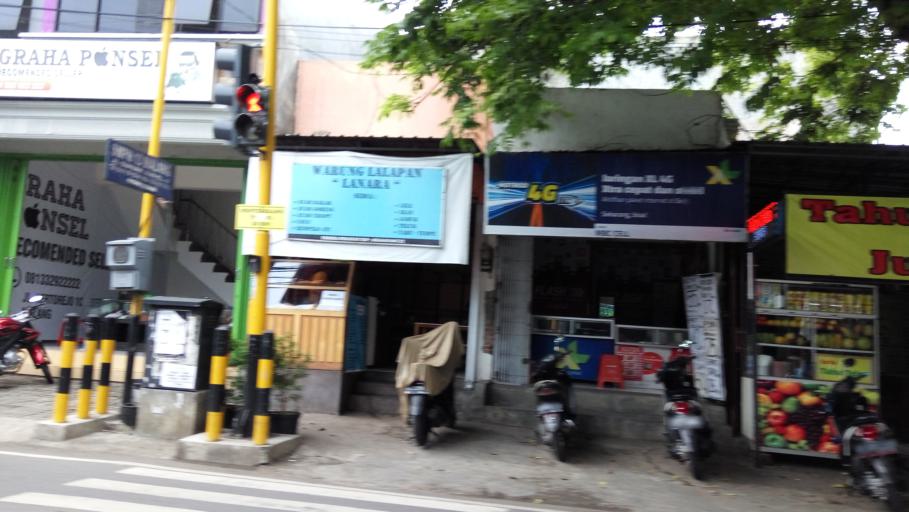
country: ID
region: East Java
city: Malang
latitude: -7.9502
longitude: 112.6090
